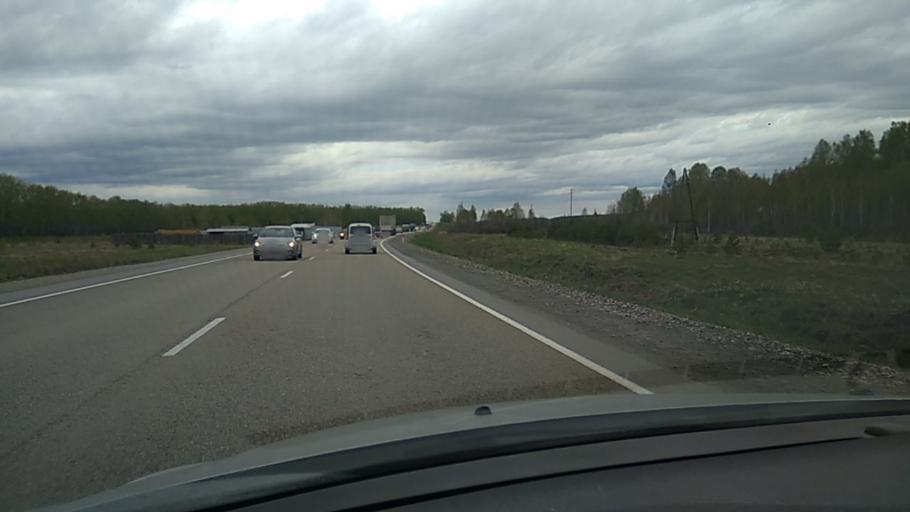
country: RU
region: Sverdlovsk
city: Dvurechensk
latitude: 56.6585
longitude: 61.1741
